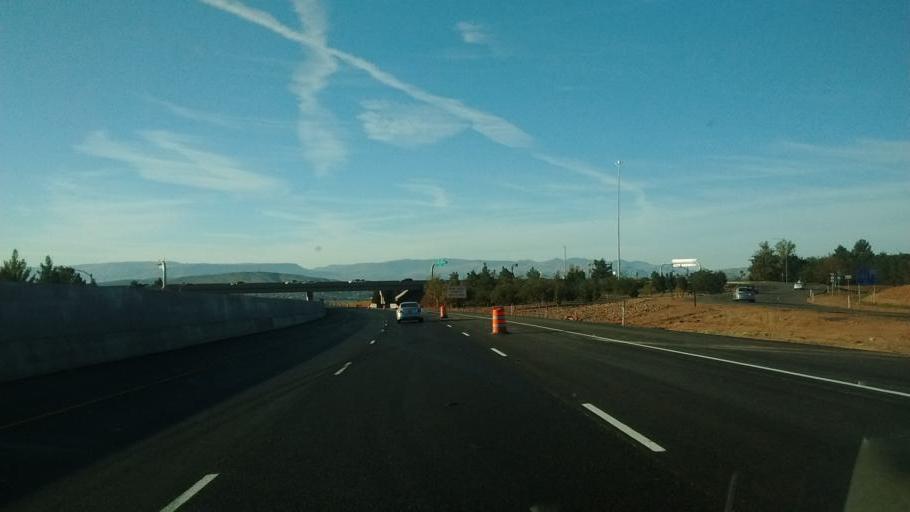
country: US
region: Utah
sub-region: Washington County
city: Saint George
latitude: 37.1120
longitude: -113.5570
